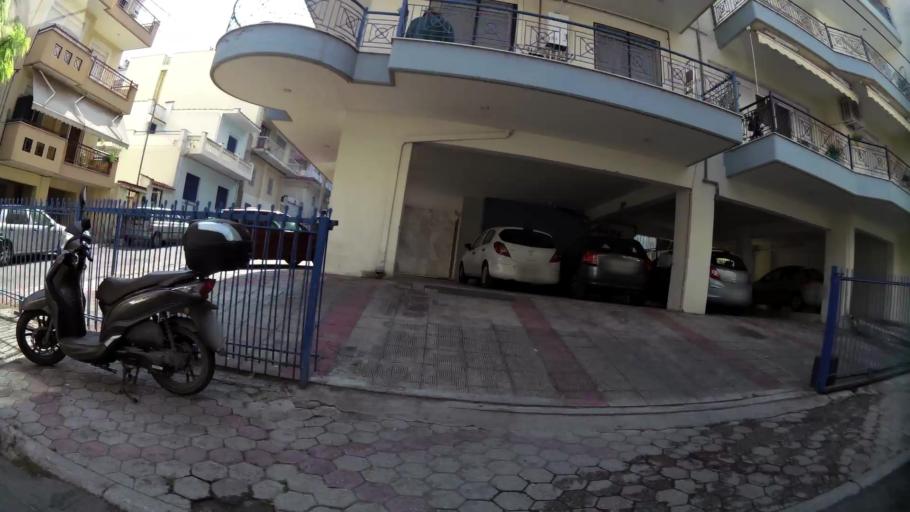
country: GR
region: Central Macedonia
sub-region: Nomos Thessalonikis
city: Sykies
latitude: 40.6489
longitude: 22.9508
